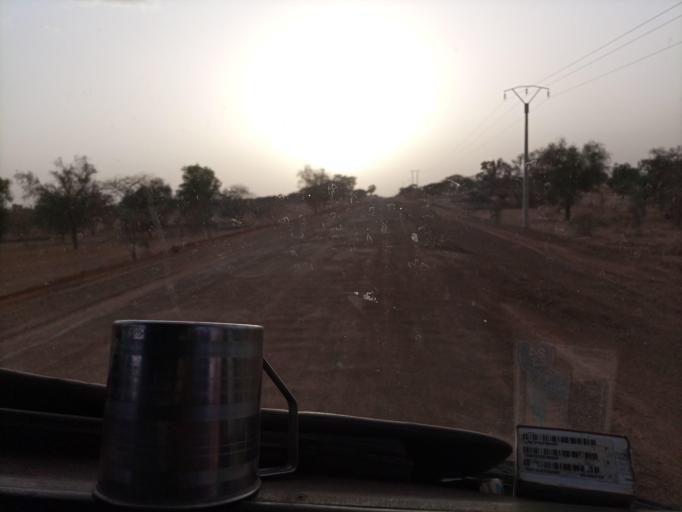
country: SN
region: Louga
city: Dara
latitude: 15.3952
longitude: -15.6437
